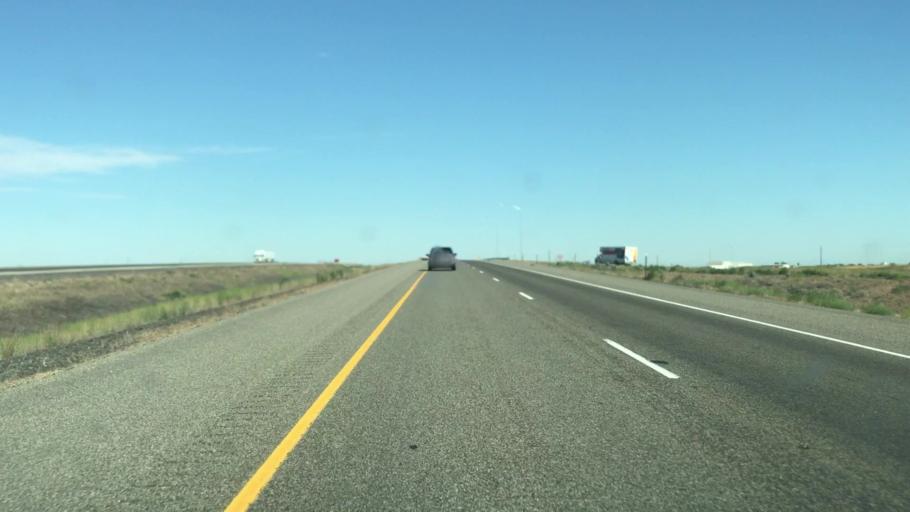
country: US
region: Idaho
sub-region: Twin Falls County
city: Twin Falls
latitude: 42.6407
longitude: -114.4410
